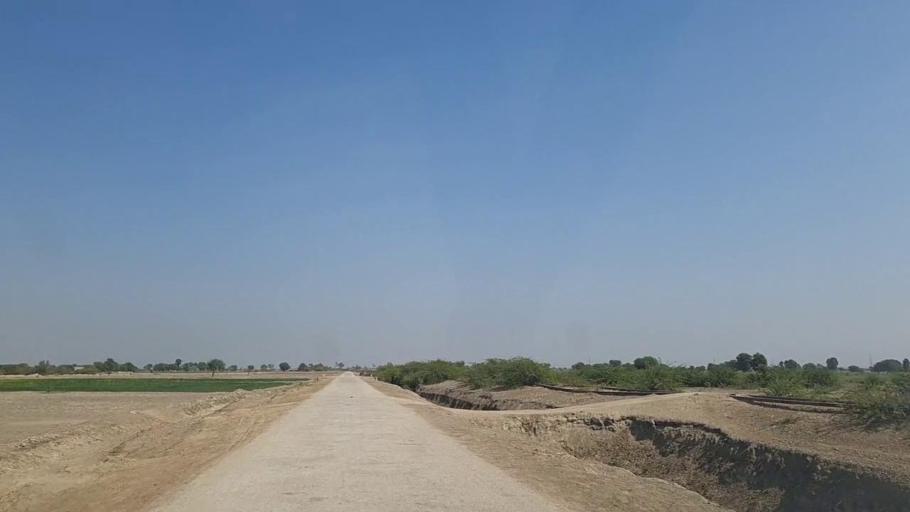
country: PK
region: Sindh
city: Naukot
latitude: 24.8706
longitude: 69.4230
